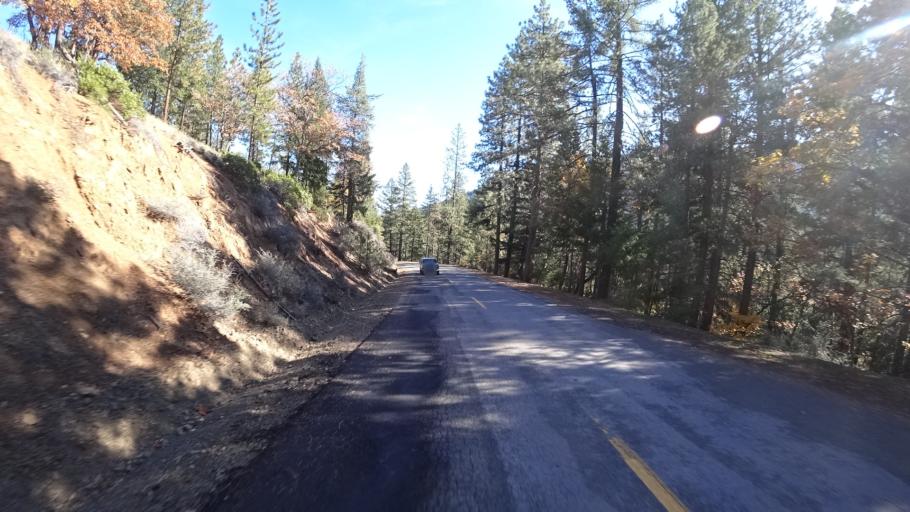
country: US
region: California
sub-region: Siskiyou County
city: Yreka
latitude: 41.7302
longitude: -122.7225
